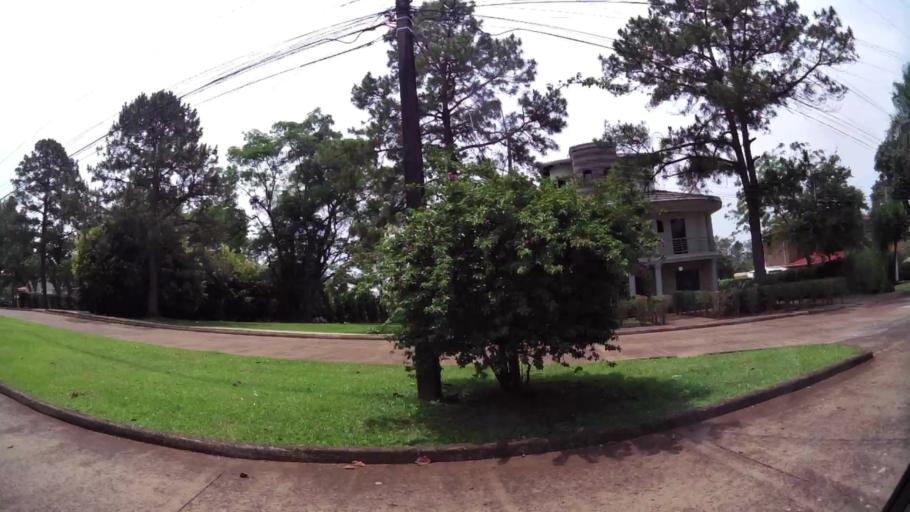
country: PY
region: Alto Parana
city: Ciudad del Este
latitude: -25.4957
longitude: -54.6107
